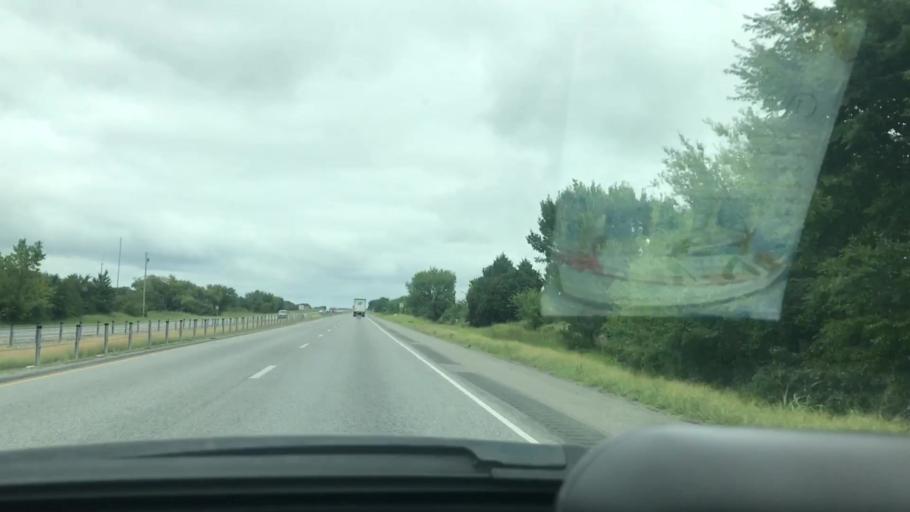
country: US
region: Oklahoma
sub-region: Pittsburg County
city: McAlester
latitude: 34.7422
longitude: -95.8973
